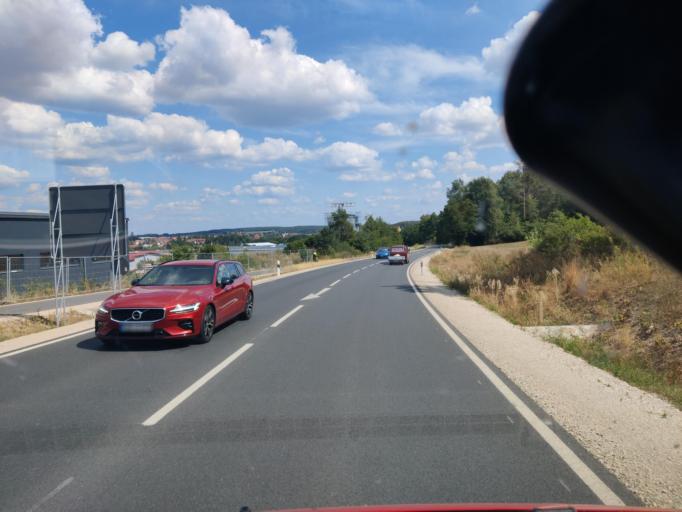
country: DE
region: Bavaria
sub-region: Regierungsbezirk Mittelfranken
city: Hilpoltstein
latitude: 49.1781
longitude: 11.1822
